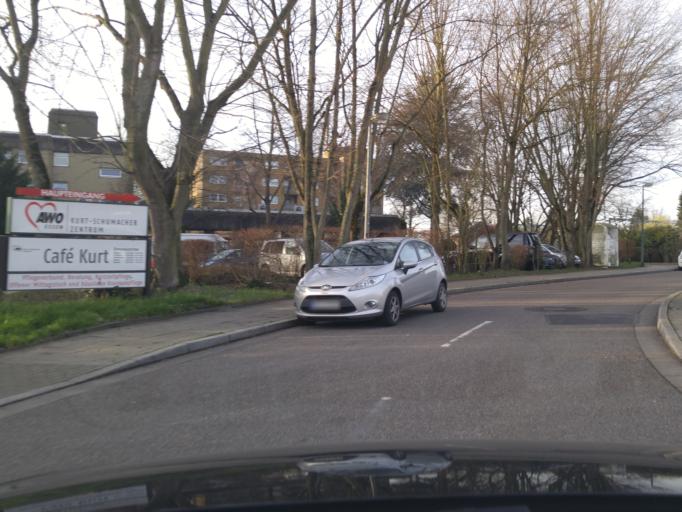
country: DE
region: North Rhine-Westphalia
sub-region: Regierungsbezirk Dusseldorf
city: Essen
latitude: 51.4194
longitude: 7.0736
